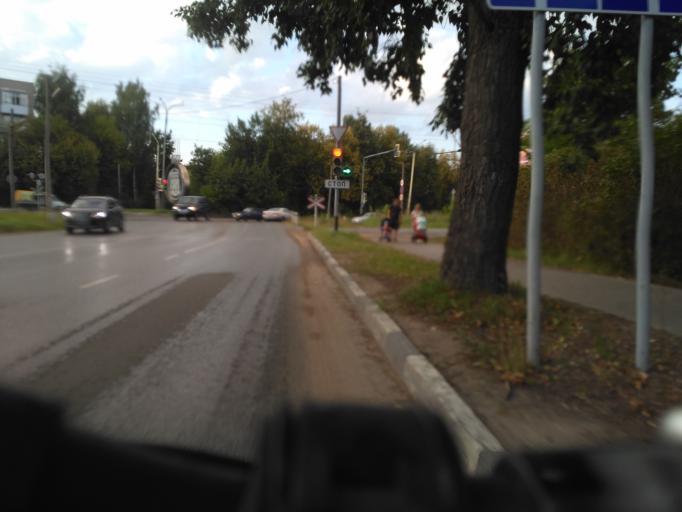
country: RU
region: Moskovskaya
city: Dubna
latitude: 56.7433
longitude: 37.1787
